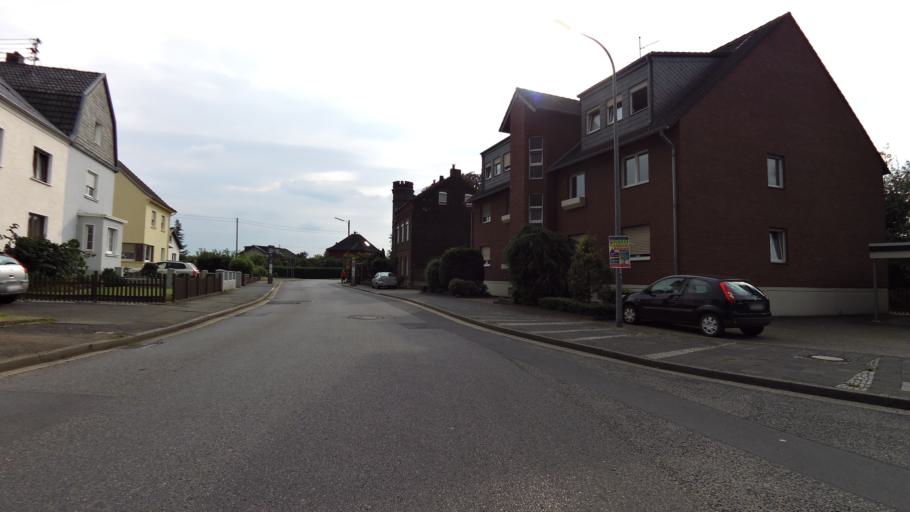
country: DE
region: North Rhine-Westphalia
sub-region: Regierungsbezirk Koln
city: Euskirchen
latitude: 50.6544
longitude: 6.8342
